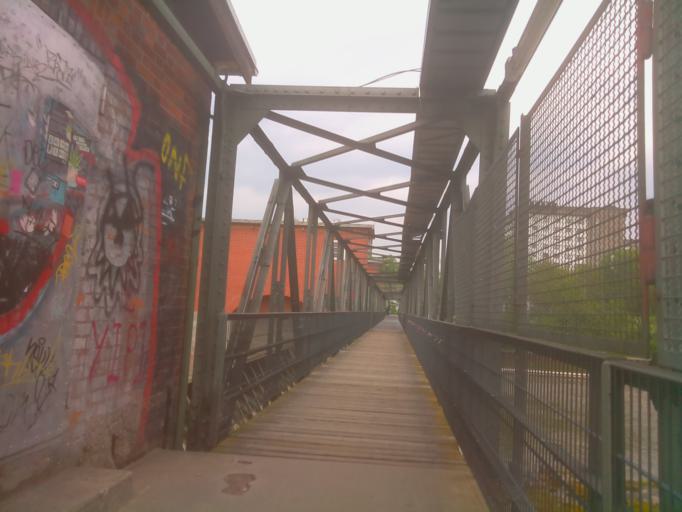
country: DE
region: Baden-Wuerttemberg
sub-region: Karlsruhe Region
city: Heidelberg
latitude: 49.4106
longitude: 8.6681
